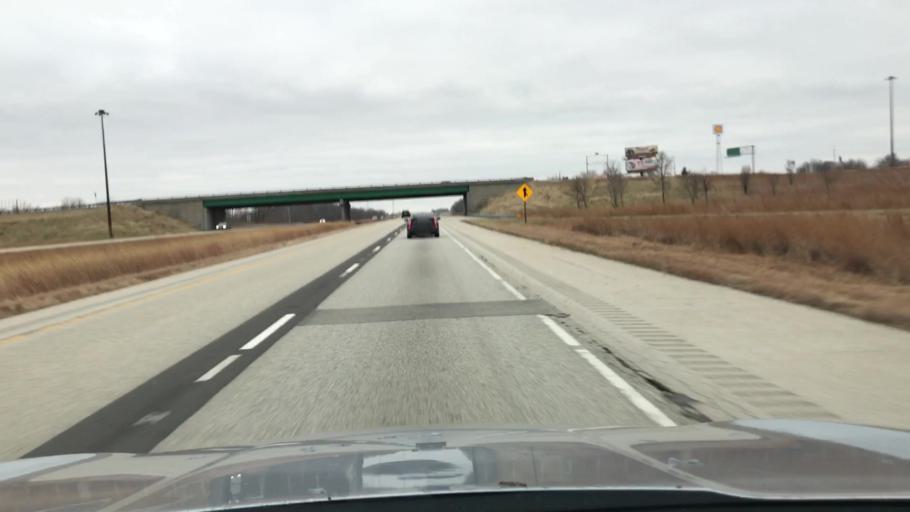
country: US
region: Illinois
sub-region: Sangamon County
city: Divernon
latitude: 39.4467
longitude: -89.6443
